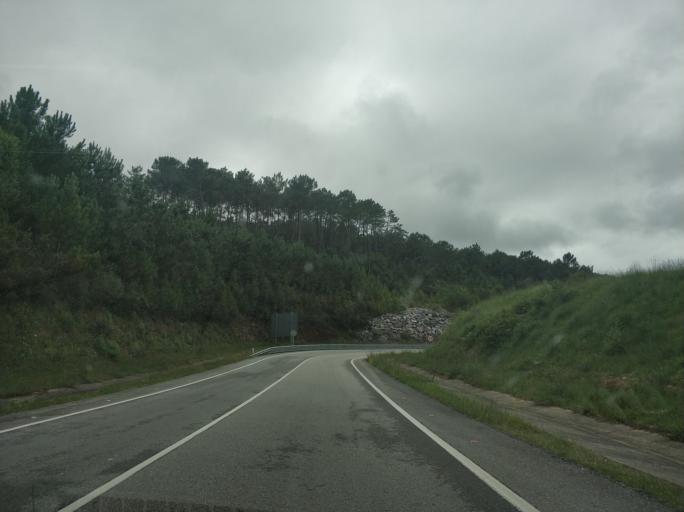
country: ES
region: Asturias
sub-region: Province of Asturias
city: Cudillero
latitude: 43.5564
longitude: -6.2834
